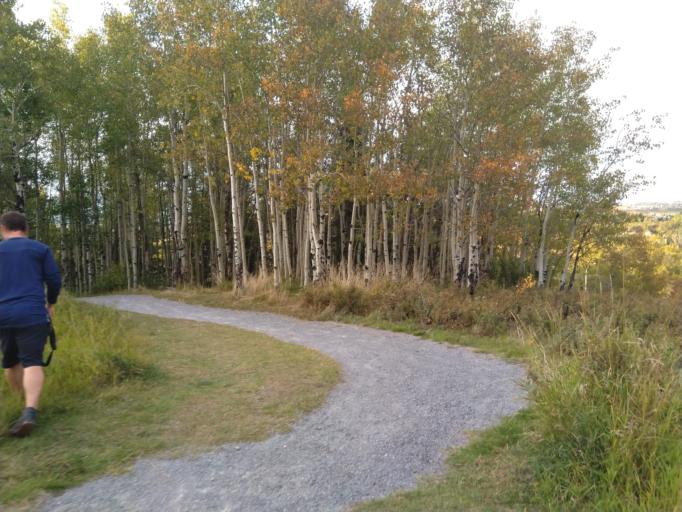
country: CA
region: Alberta
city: Cochrane
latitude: 51.1839
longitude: -114.5021
